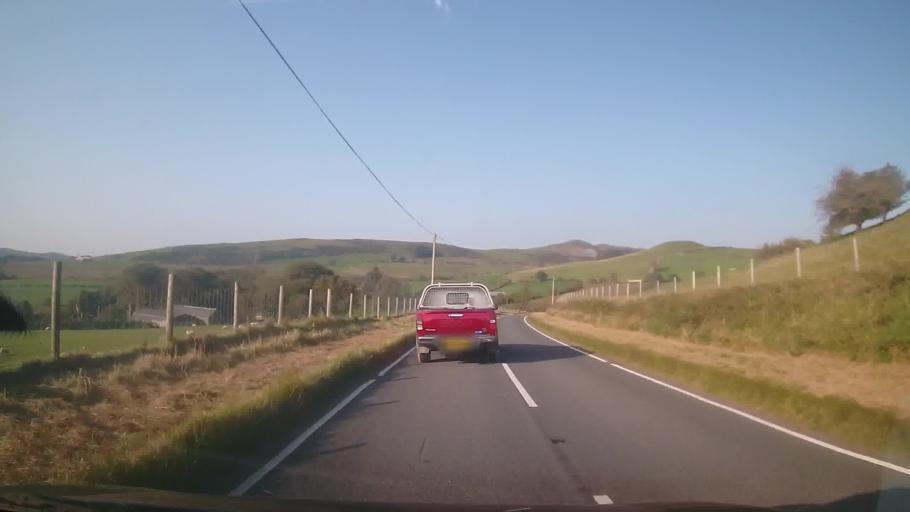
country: GB
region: Wales
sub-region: County of Ceredigion
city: Lledrod
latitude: 52.3044
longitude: -3.8517
